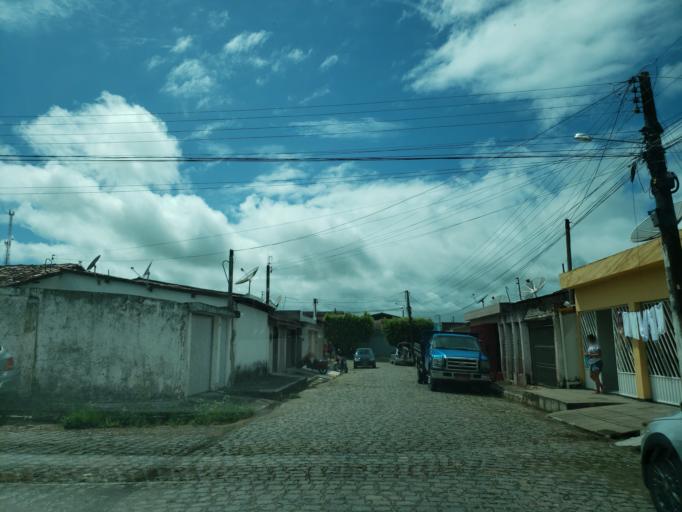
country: BR
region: Alagoas
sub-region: Uniao Dos Palmares
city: Uniao dos Palmares
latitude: -9.1597
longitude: -36.0233
